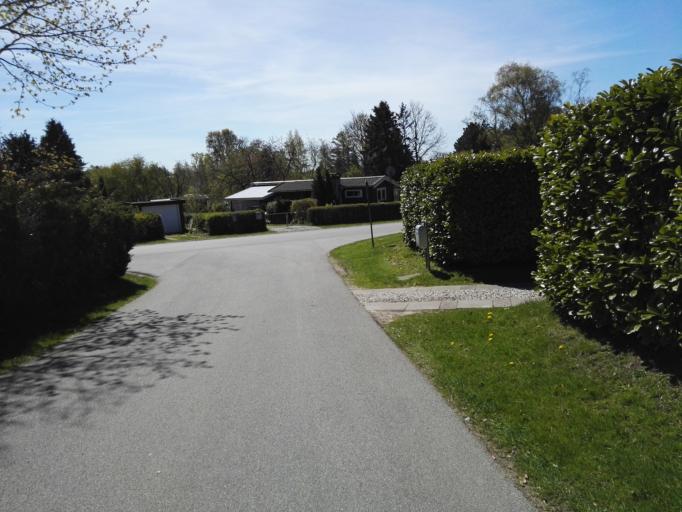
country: DK
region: Capital Region
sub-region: Frederikssund Kommune
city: Frederikssund
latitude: 55.9020
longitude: 12.0551
